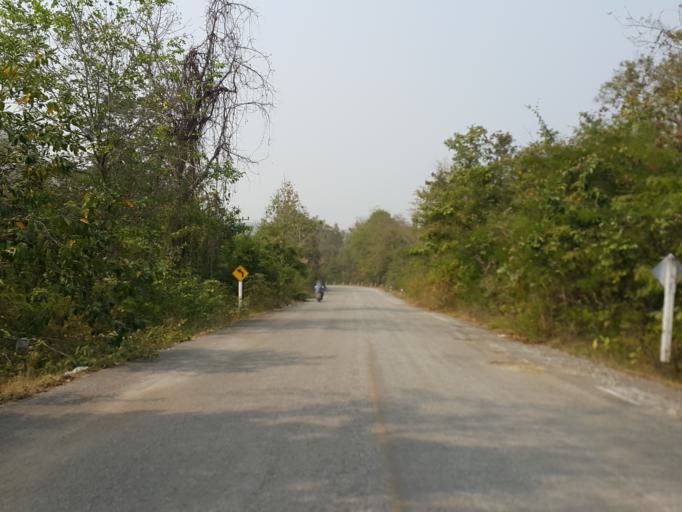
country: TH
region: Lampang
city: Mae Phrik
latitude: 17.4957
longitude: 99.0857
